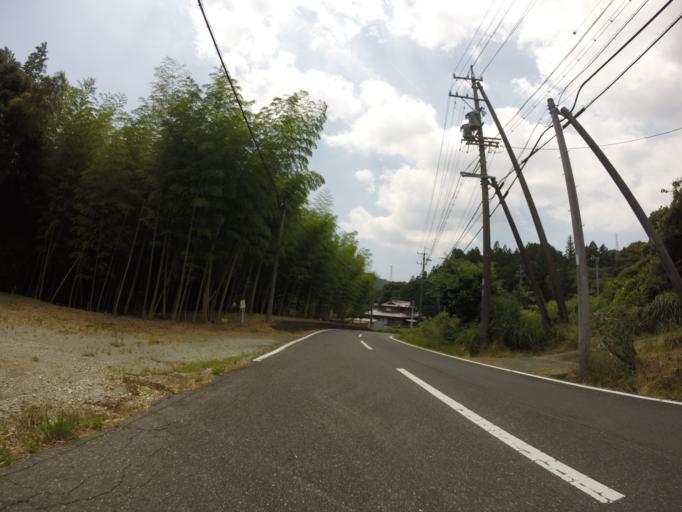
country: JP
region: Shizuoka
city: Kanaya
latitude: 34.8217
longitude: 138.0708
